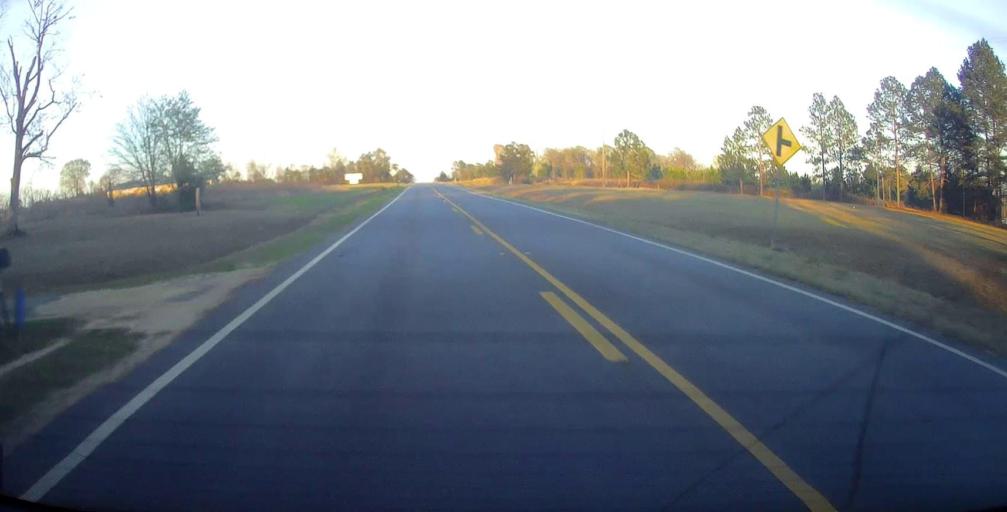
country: US
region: Georgia
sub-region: Dodge County
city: Chester
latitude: 32.3557
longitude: -83.0232
